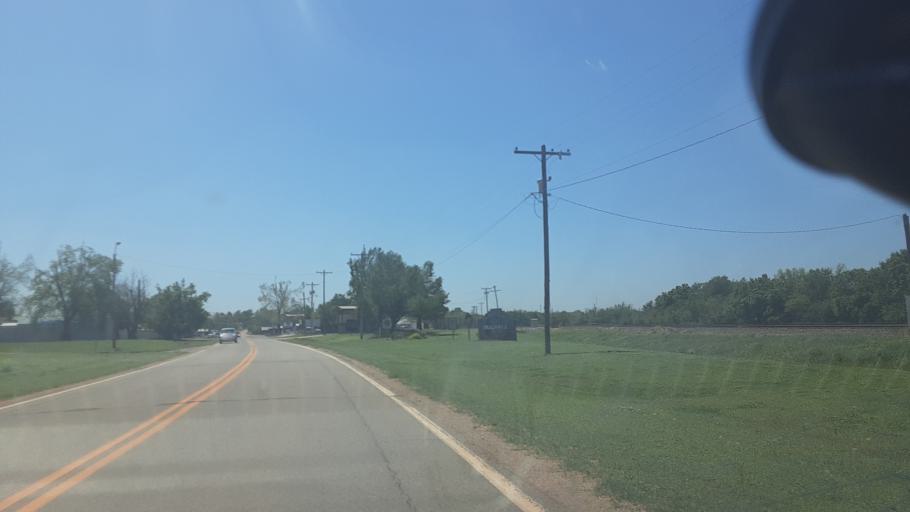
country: US
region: Oklahoma
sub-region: Logan County
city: Guthrie
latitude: 36.0677
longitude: -97.4070
